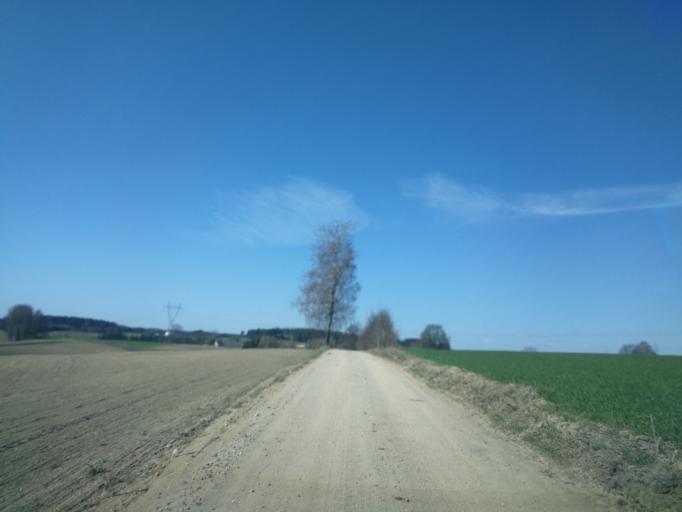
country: PL
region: Warmian-Masurian Voivodeship
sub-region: Powiat dzialdowski
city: Rybno
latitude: 53.4383
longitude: 19.9500
